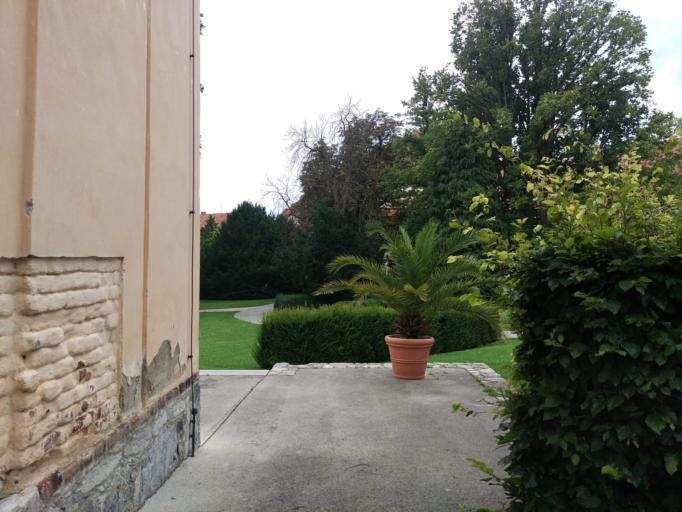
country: AT
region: Styria
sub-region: Graz Stadt
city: Graz
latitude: 47.0734
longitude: 15.4435
